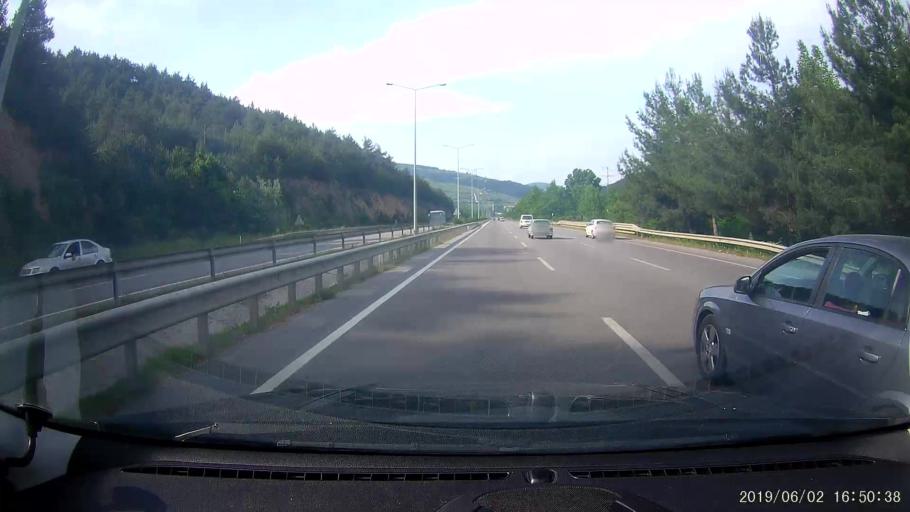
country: TR
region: Samsun
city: Taflan
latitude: 41.2584
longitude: 36.1742
